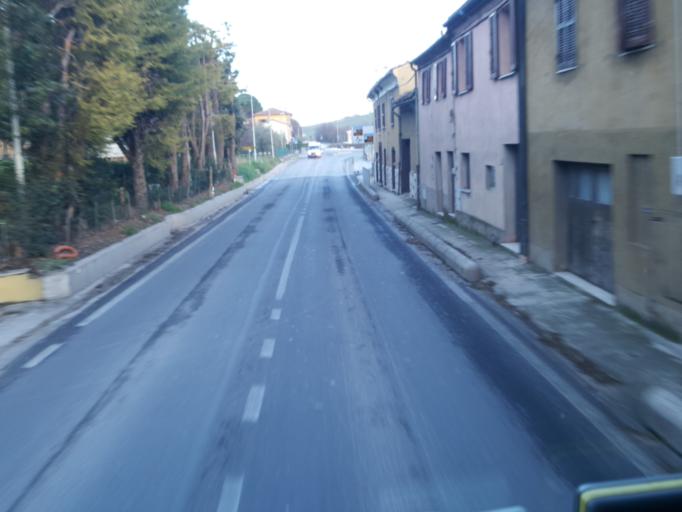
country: IT
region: The Marches
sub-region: Provincia di Macerata
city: San Severino Marche
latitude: 43.2406
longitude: 13.2170
